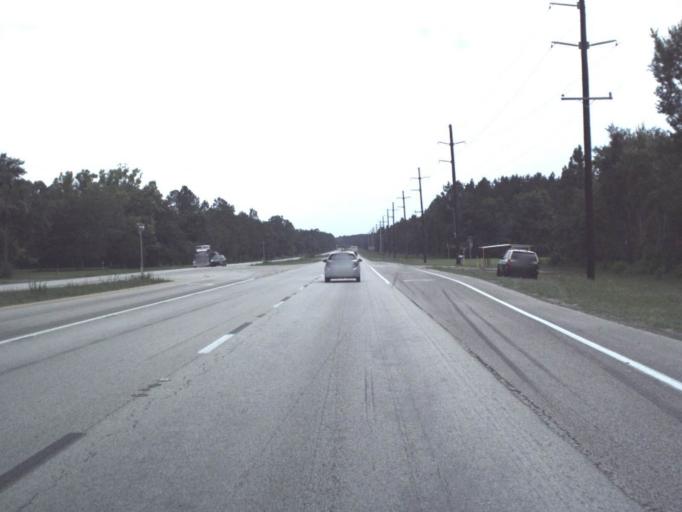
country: US
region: Florida
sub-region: Bradford County
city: Starke
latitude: 30.1005
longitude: -82.0540
